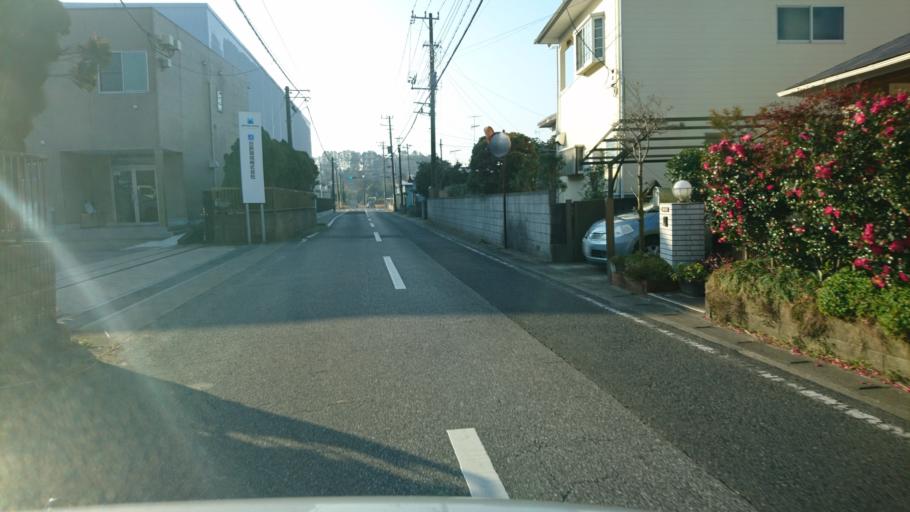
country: JP
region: Chiba
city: Kimitsu
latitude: 35.3051
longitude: 139.9473
